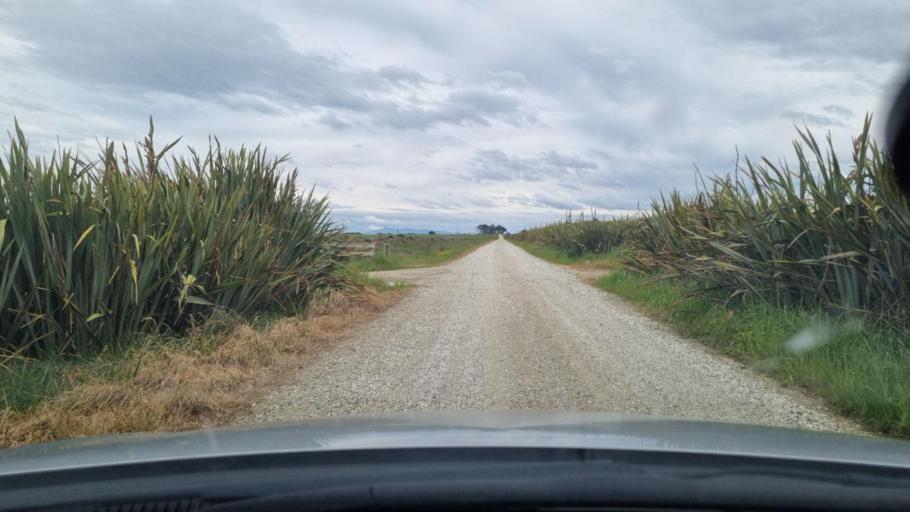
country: NZ
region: Southland
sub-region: Invercargill City
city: Invercargill
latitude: -46.3928
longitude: 168.2724
